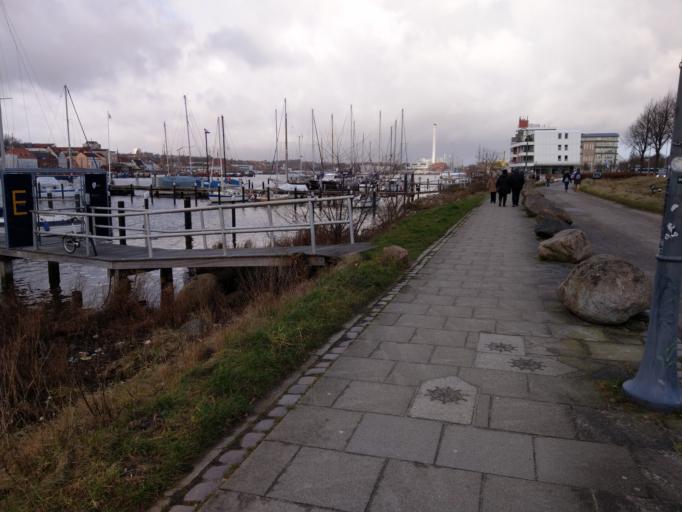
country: DE
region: Schleswig-Holstein
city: Flensburg
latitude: 54.7914
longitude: 9.4379
